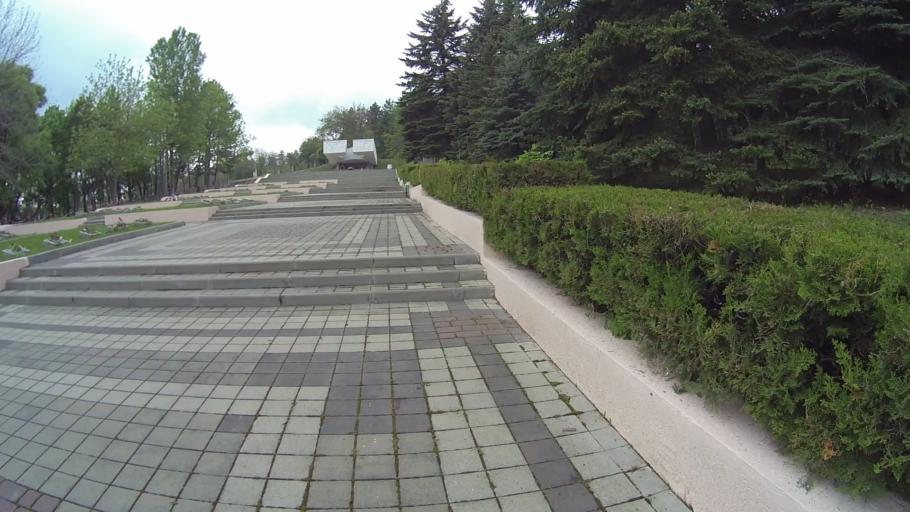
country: RU
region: Stavropol'skiy
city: Pyatigorsk
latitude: 44.0468
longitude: 43.0757
